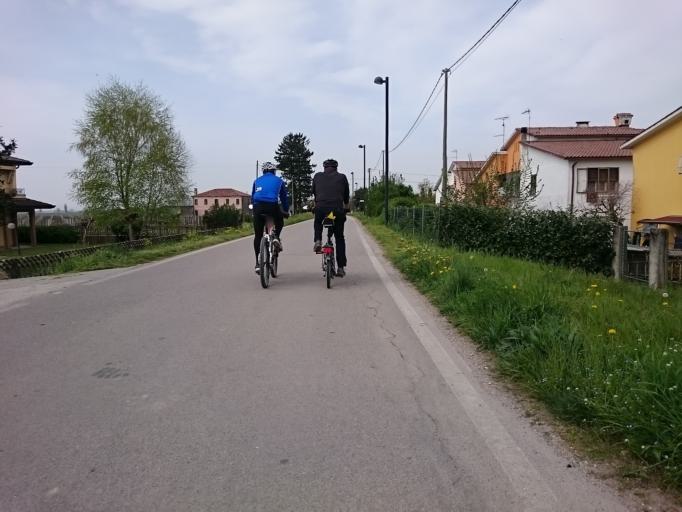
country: IT
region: Veneto
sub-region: Provincia di Padova
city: Bagnoli di Sopra
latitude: 45.1673
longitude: 11.8489
